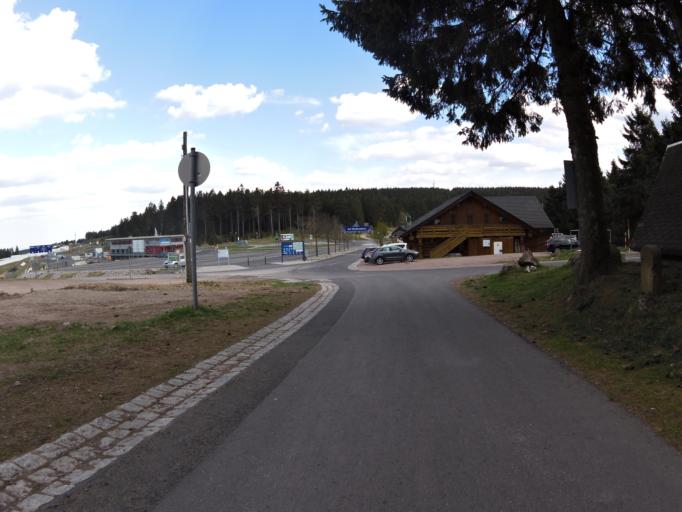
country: DE
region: Thuringia
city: Oberhof
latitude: 50.7061
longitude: 10.6917
